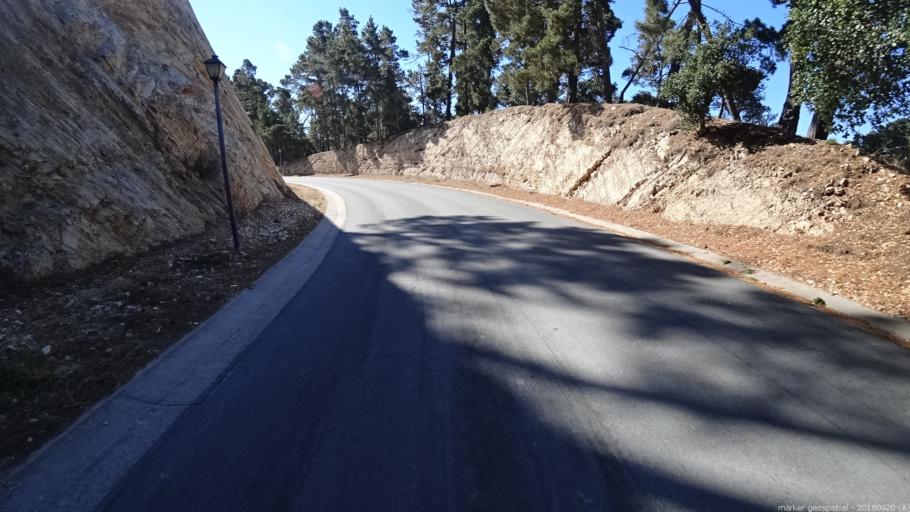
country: US
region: California
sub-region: Monterey County
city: Carmel-by-the-Sea
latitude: 36.5591
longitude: -121.8971
